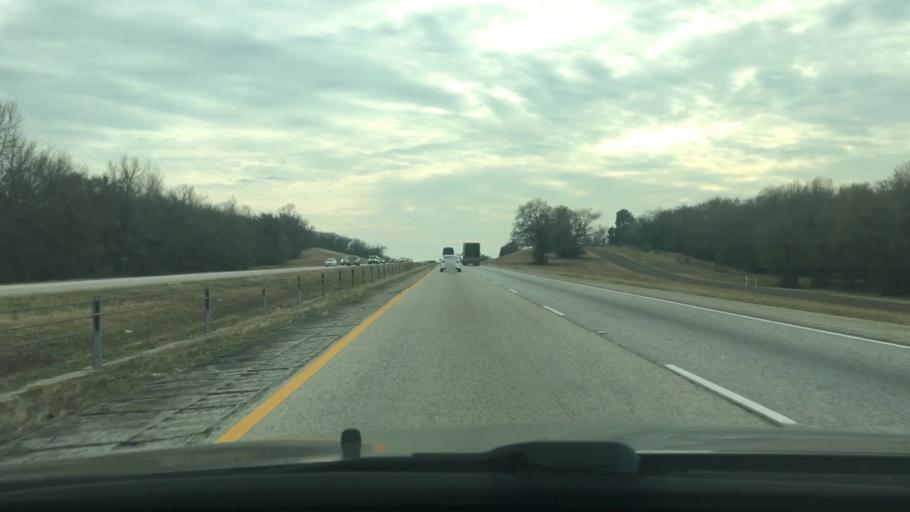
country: US
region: Texas
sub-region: Leon County
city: Centerville
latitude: 31.2276
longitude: -95.9950
